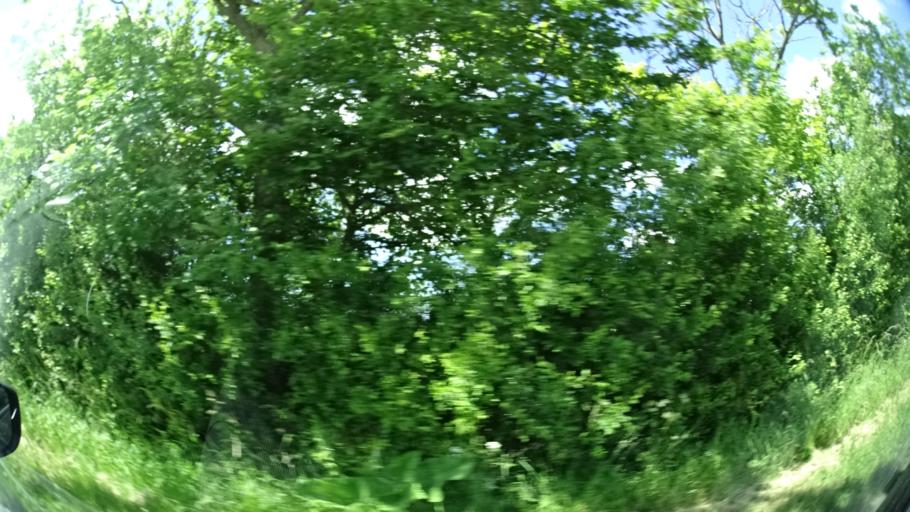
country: DK
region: Central Jutland
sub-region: Syddjurs Kommune
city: Ronde
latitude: 56.2929
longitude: 10.4808
